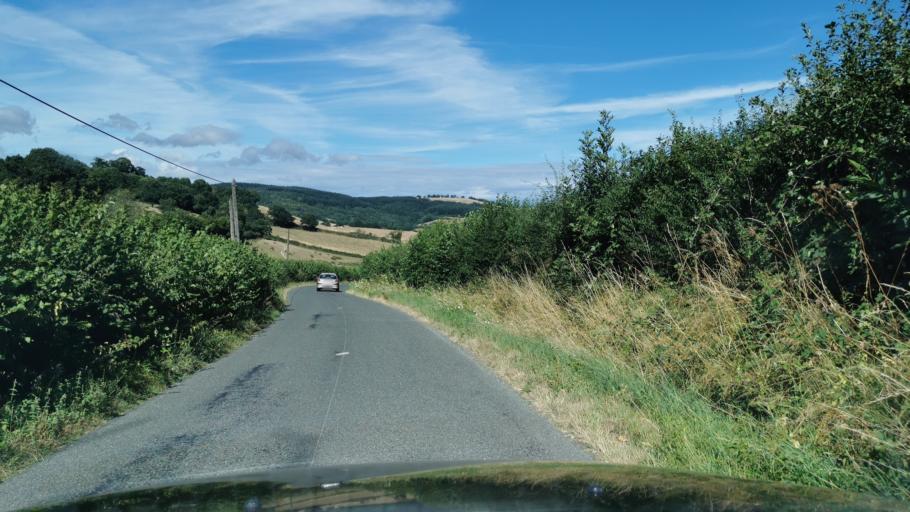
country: FR
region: Bourgogne
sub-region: Departement de Saone-et-Loire
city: Marmagne
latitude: 46.8057
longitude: 4.3164
